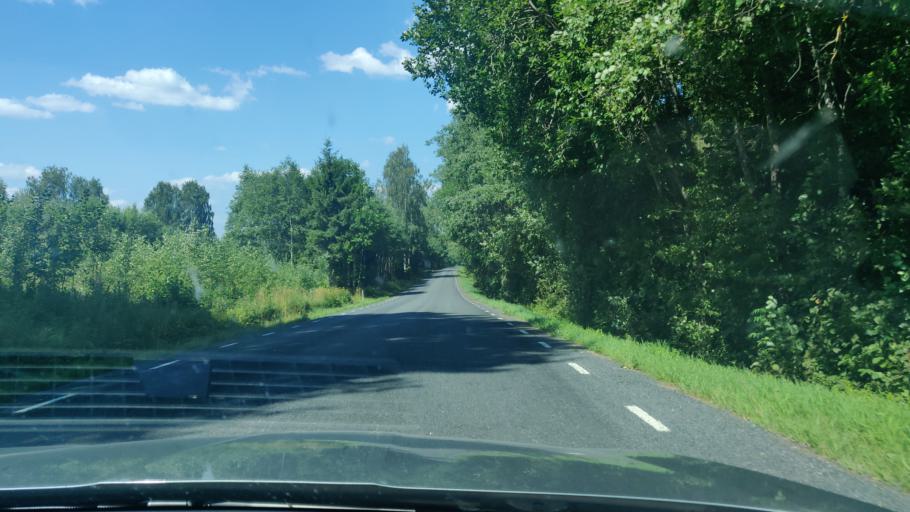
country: EE
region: Tartu
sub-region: Elva linn
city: Elva
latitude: 58.1527
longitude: 26.4720
